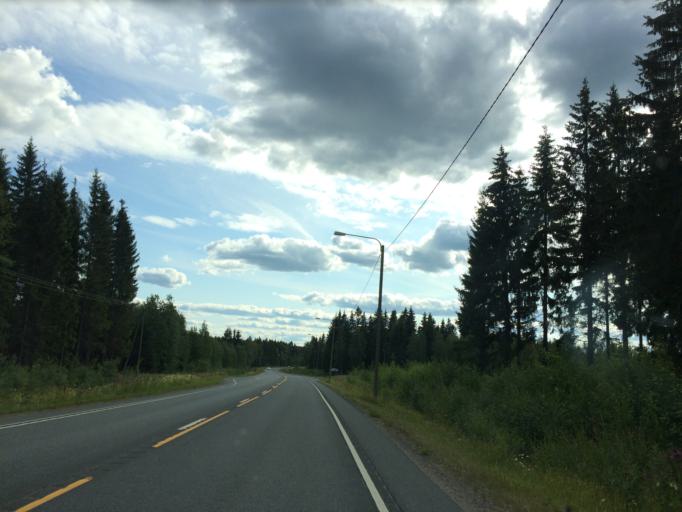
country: FI
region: Haeme
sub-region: Haemeenlinna
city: Janakkala
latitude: 60.9190
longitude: 24.5743
